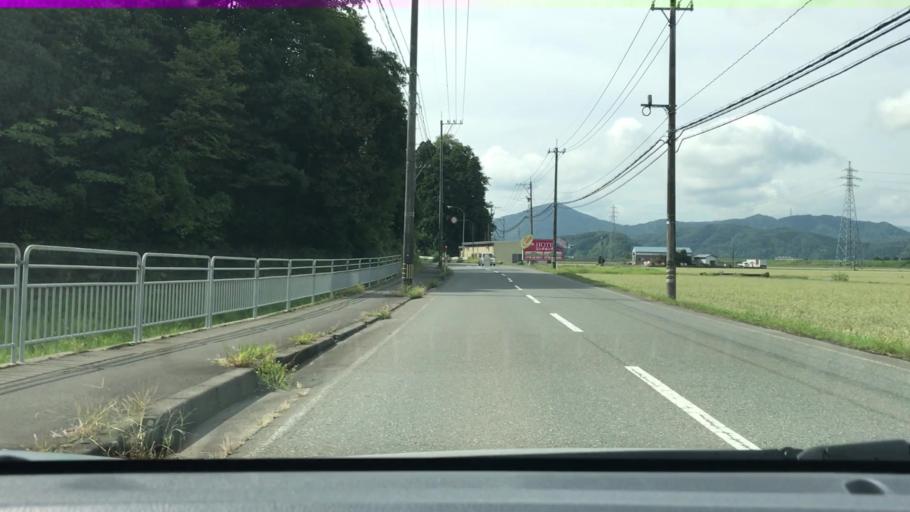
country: JP
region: Fukui
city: Fukui-shi
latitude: 36.0215
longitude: 136.1769
